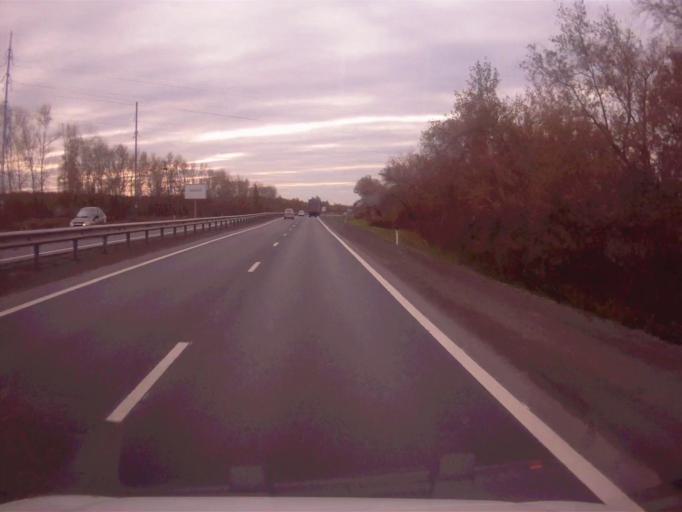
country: RU
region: Chelyabinsk
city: Roza
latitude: 54.9854
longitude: 61.4332
